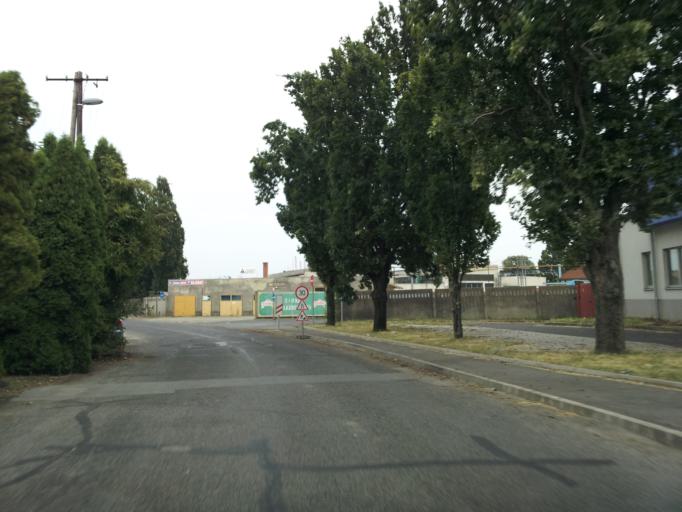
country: HU
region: Vas
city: Szombathely
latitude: 47.2344
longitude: 16.6382
